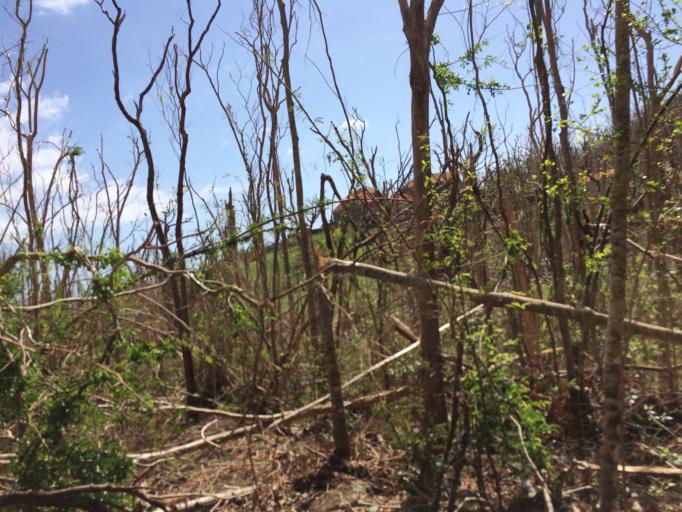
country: DM
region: Saint John
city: Portsmouth
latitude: 15.5846
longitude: -61.4724
